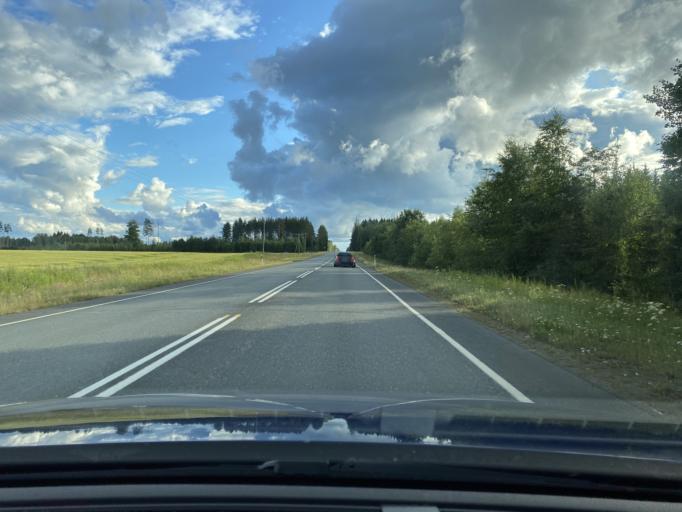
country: FI
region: Haeme
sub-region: Haemeenlinna
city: Renko
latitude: 60.8857
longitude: 24.2481
